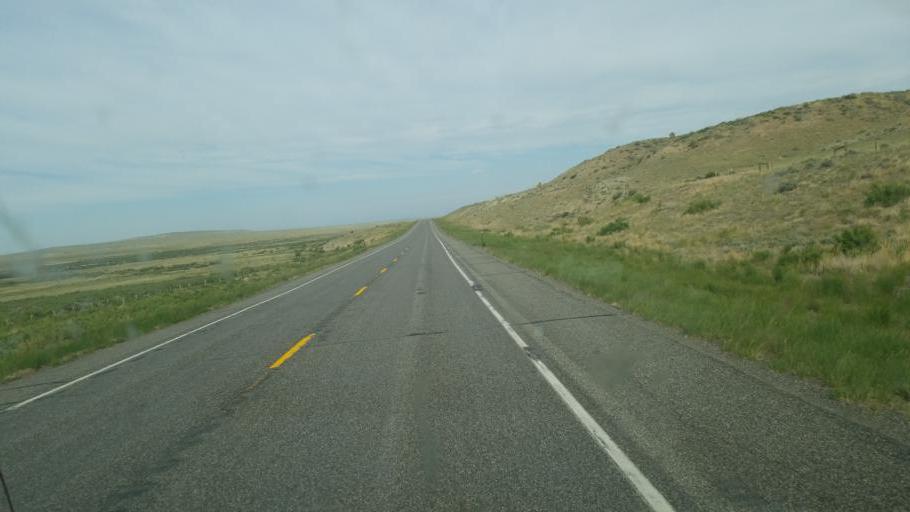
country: US
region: Wyoming
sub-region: Fremont County
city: Riverton
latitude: 43.2213
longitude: -107.9937
